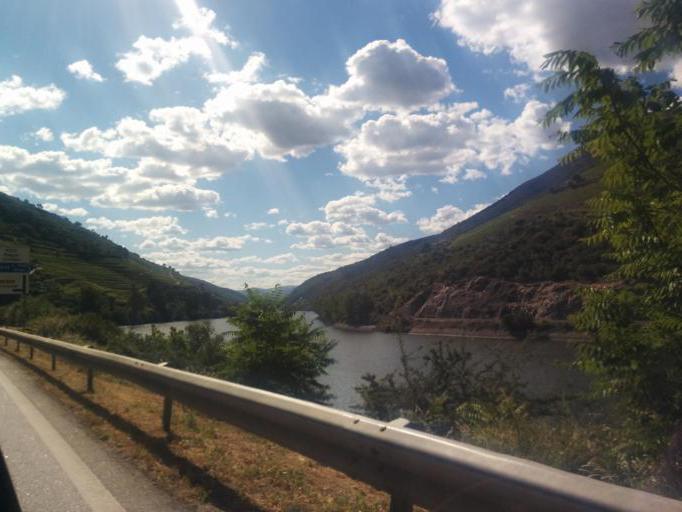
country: PT
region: Viseu
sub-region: Armamar
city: Armamar
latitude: 41.1414
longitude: -7.6945
